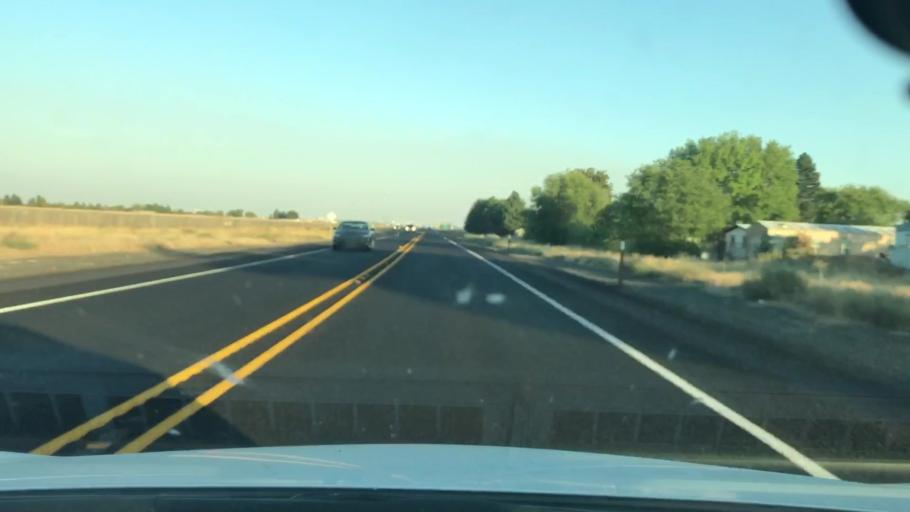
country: US
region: Washington
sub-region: Grant County
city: Cascade Valley
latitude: 47.1599
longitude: -119.3204
